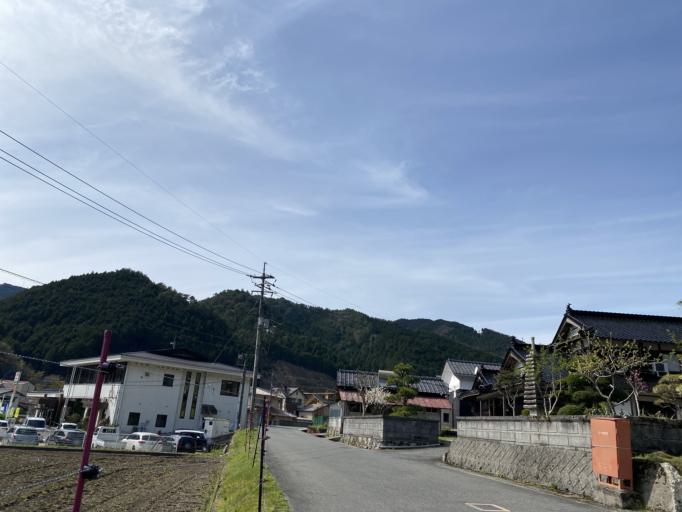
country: JP
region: Hyogo
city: Yamazakicho-nakabirose
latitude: 35.1703
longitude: 134.3370
